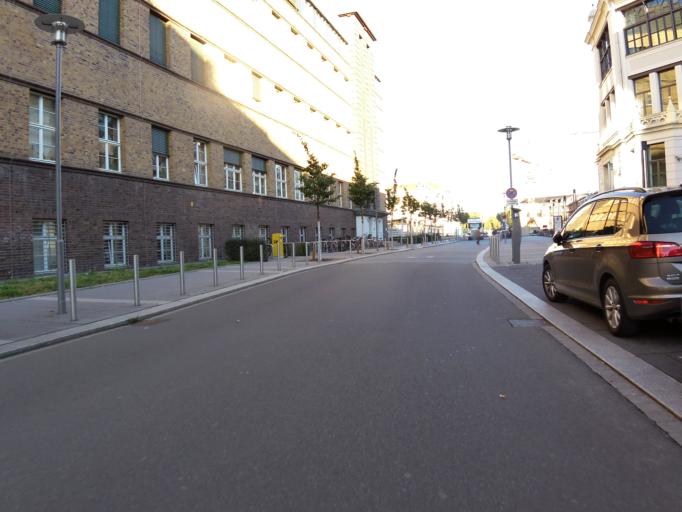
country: DE
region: Saxony
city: Leipzig
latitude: 51.3315
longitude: 12.3877
